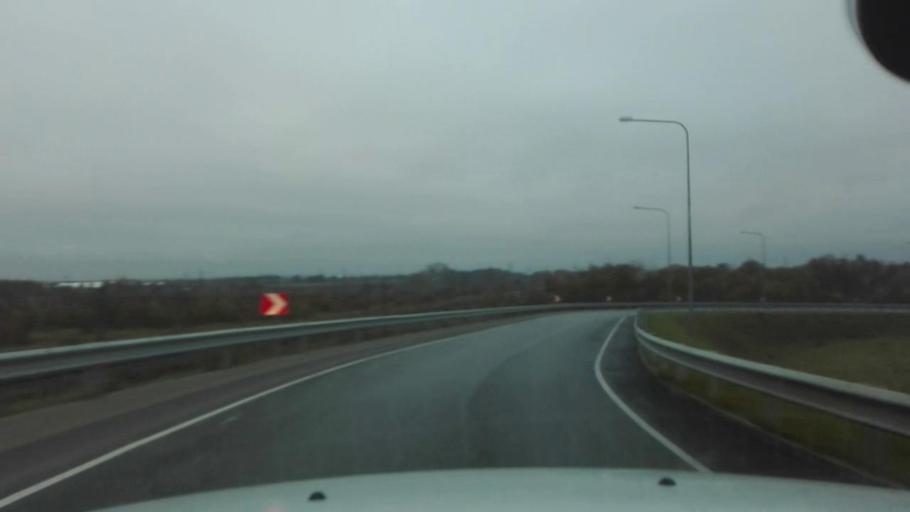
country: EE
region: Harju
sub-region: Maardu linn
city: Maardu
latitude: 59.4568
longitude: 24.9890
